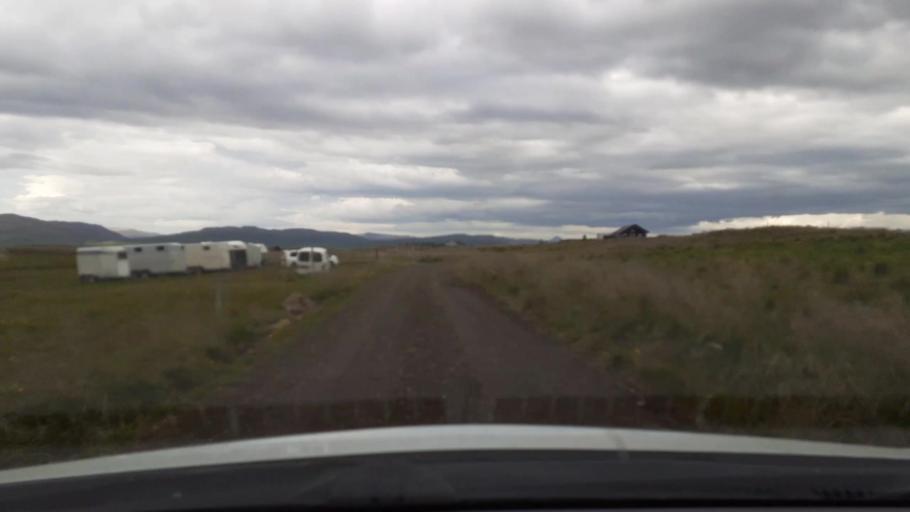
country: IS
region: West
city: Borgarnes
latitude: 64.6535
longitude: -21.8794
